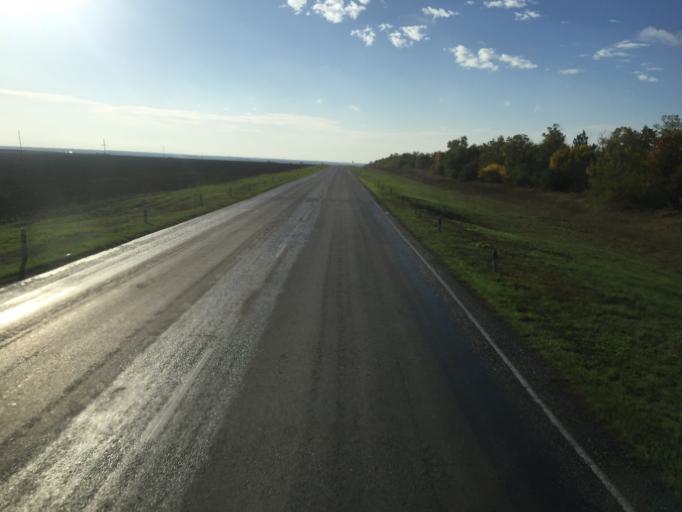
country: RU
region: Rostov
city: Mechetinskaya
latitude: 46.6832
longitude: 40.5203
